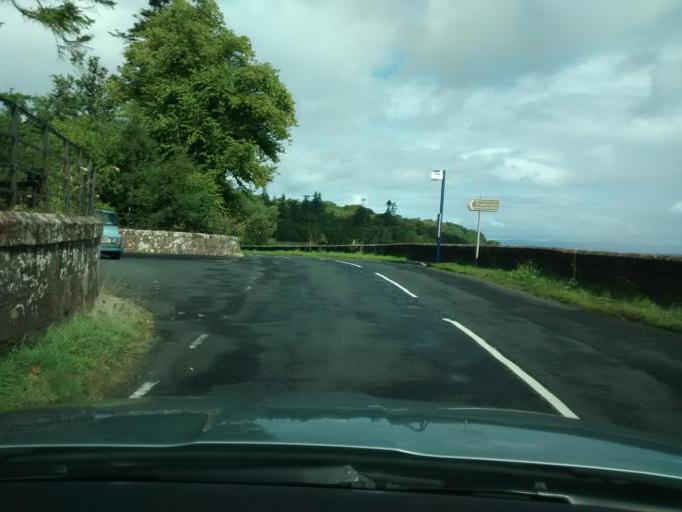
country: GB
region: Scotland
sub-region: North Ayrshire
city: Lamlash
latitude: 55.5939
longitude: -5.1459
